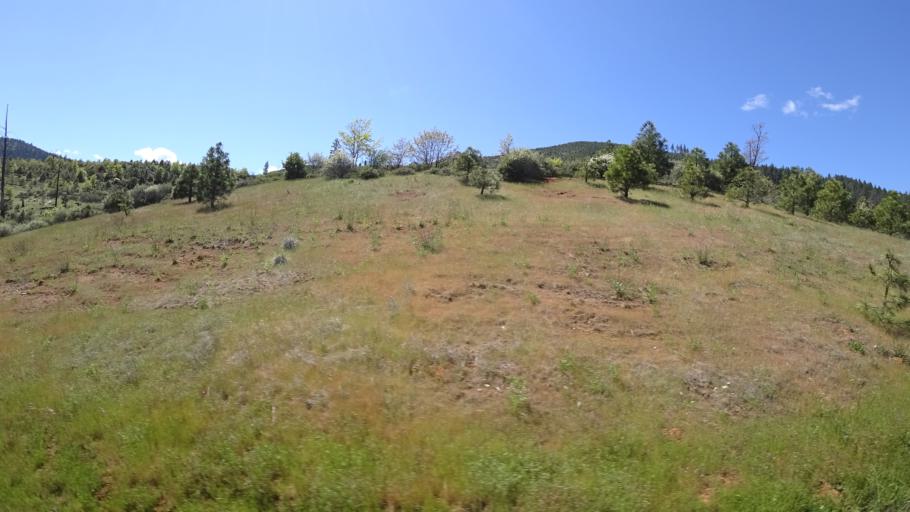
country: US
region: California
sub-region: Trinity County
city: Weaverville
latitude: 40.7455
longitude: -122.9711
